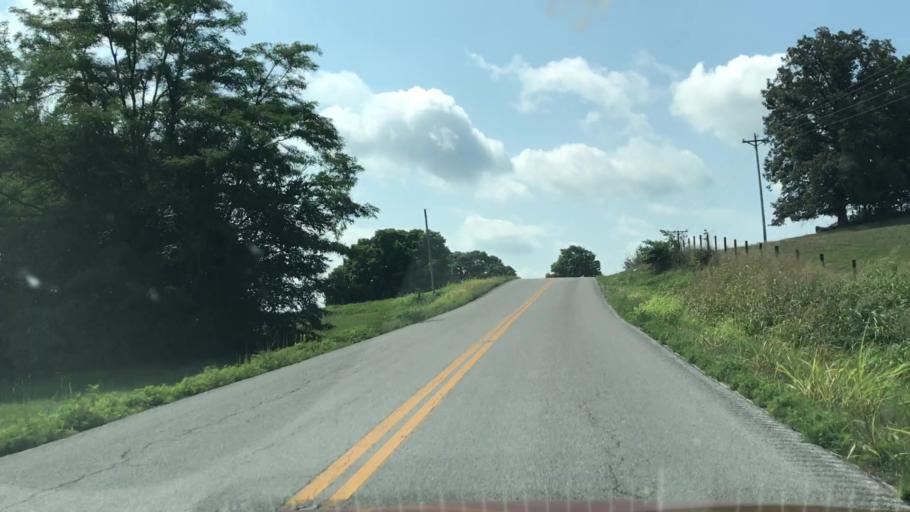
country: US
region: Kentucky
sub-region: Barren County
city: Glasgow
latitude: 36.8386
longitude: -85.8288
